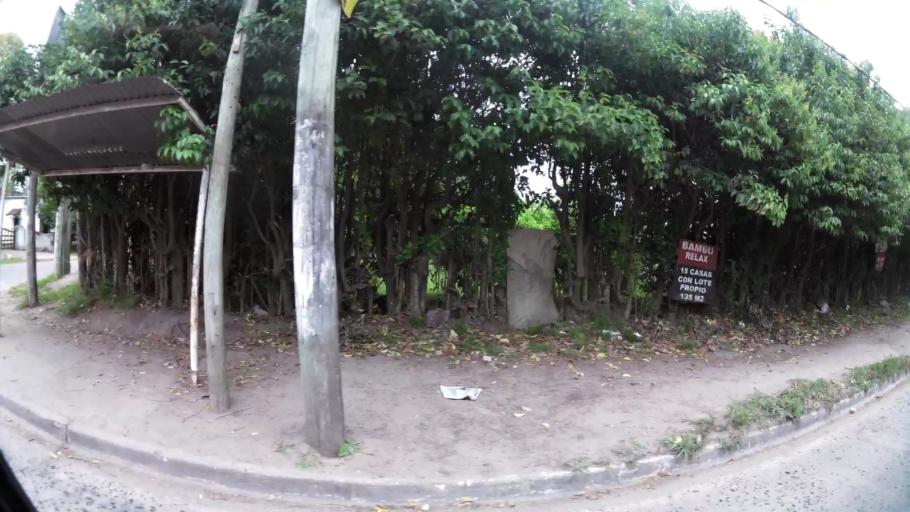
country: AR
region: Buenos Aires
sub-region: Partido de Ezeiza
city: Ezeiza
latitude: -34.8685
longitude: -58.5063
